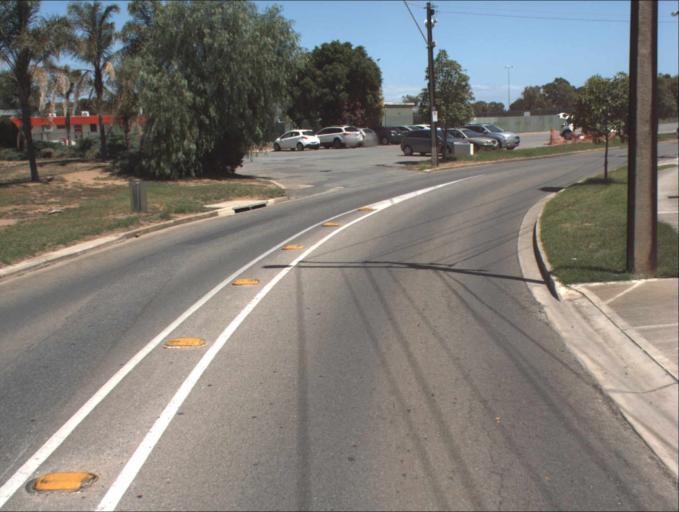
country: AU
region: South Australia
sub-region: Charles Sturt
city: Woodville North
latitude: -34.8554
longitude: 138.5624
